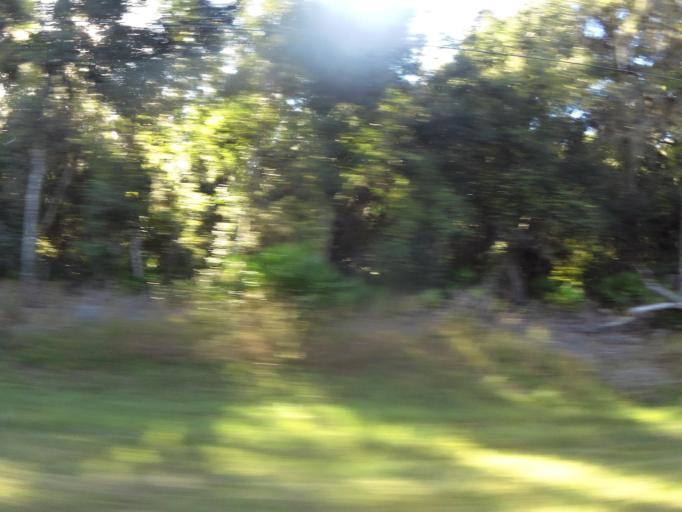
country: US
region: Florida
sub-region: Marion County
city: Citra
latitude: 29.4934
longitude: -82.1713
